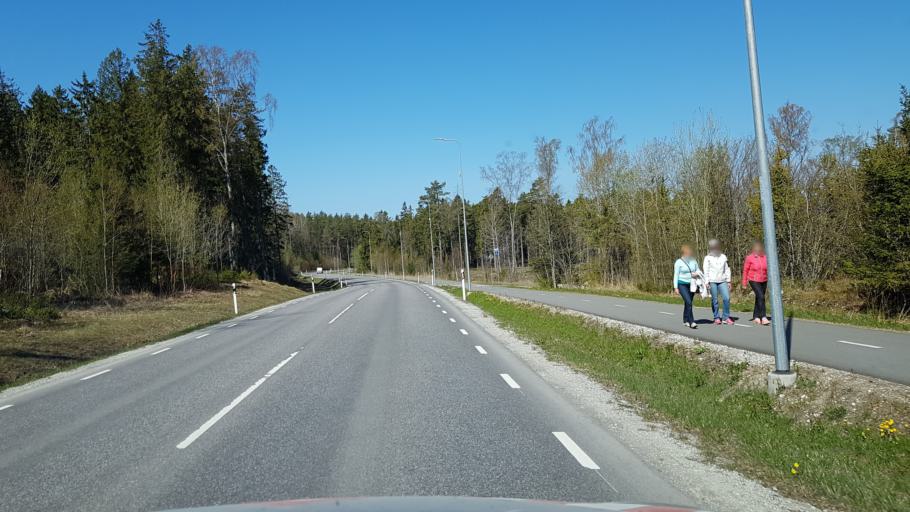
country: EE
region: Harju
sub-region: Viimsi vald
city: Viimsi
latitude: 59.5226
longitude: 24.8910
